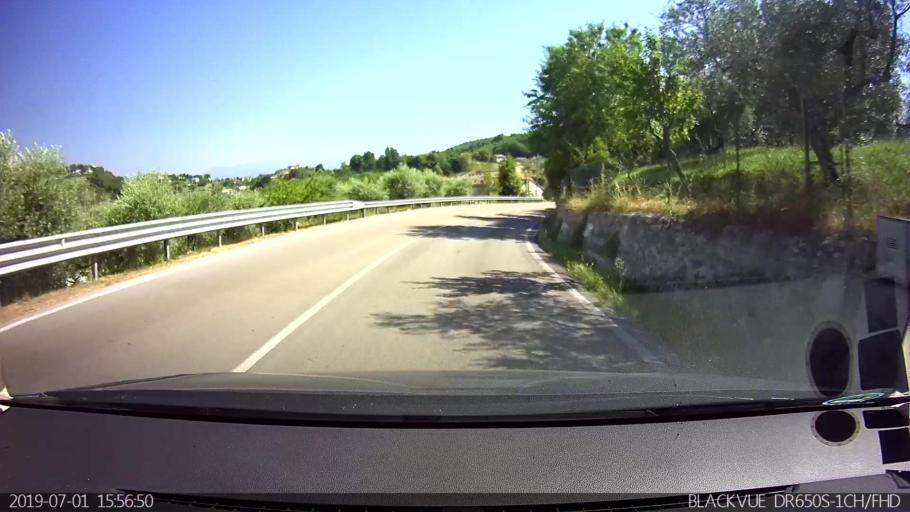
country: IT
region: Latium
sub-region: Provincia di Frosinone
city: Veroli
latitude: 41.6799
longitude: 13.4183
